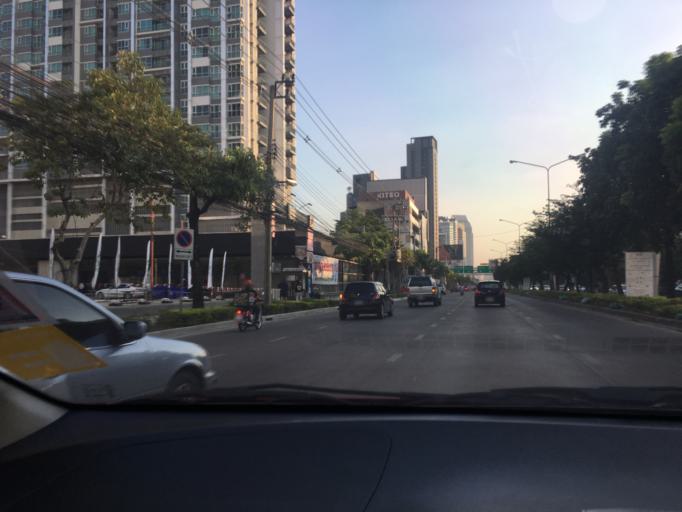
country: TH
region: Bangkok
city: Huai Khwang
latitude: 13.7841
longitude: 100.5739
